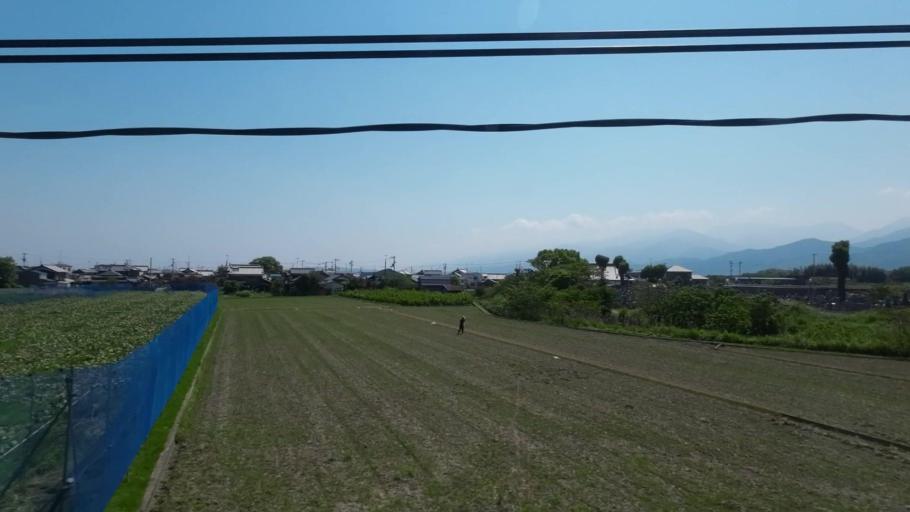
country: JP
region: Ehime
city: Saijo
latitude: 33.9097
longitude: 133.0991
